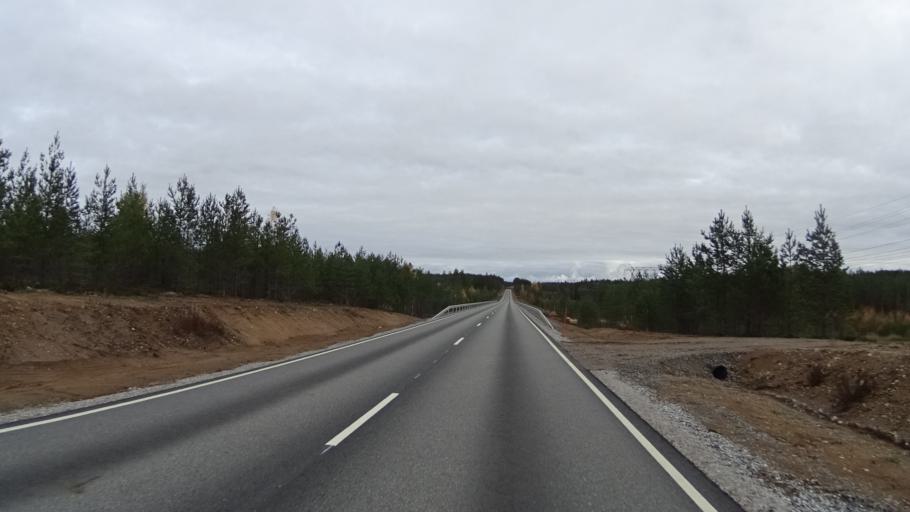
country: FI
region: South Karelia
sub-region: Lappeenranta
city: Lemi
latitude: 60.9803
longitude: 27.8965
